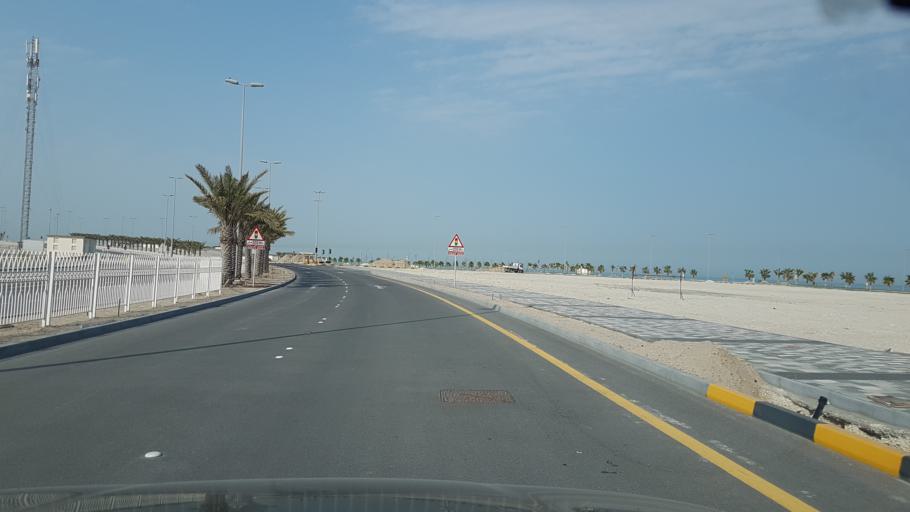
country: BH
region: Muharraq
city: Al Hadd
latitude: 26.2715
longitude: 50.6777
